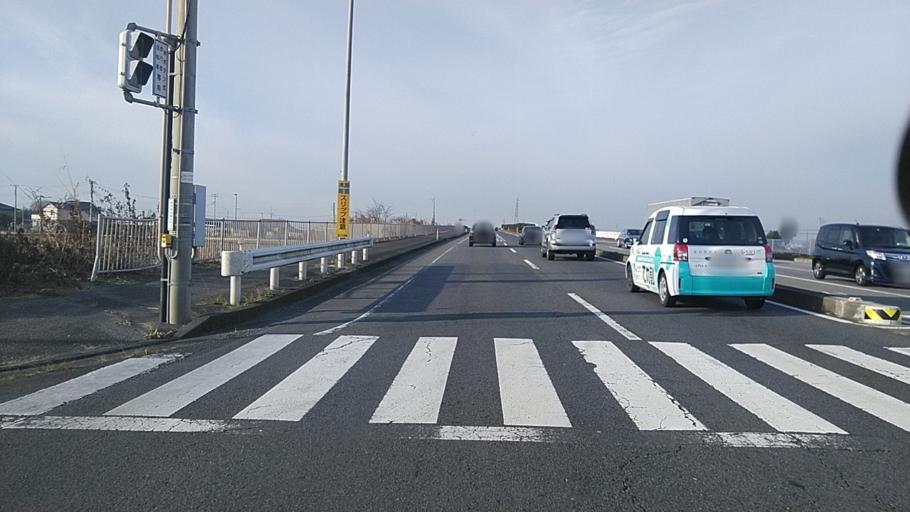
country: JP
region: Tochigi
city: Oyama
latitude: 36.3071
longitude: 139.7273
